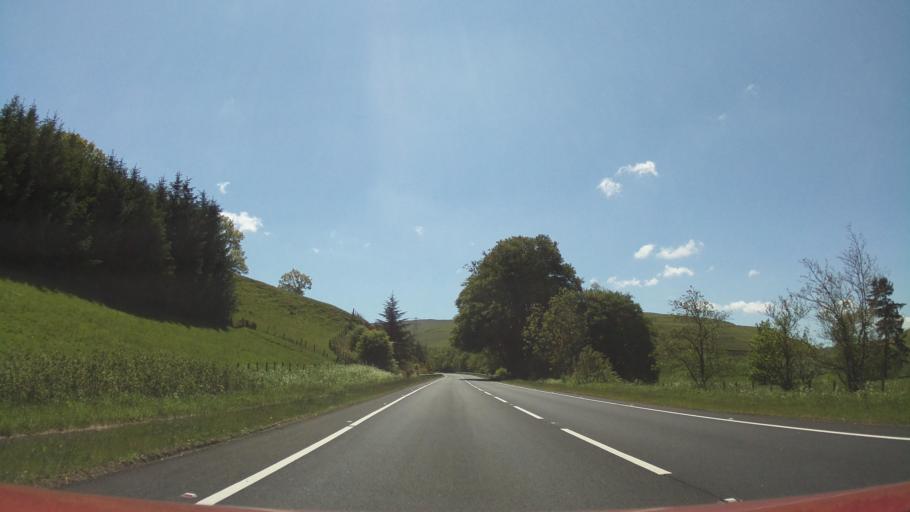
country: GB
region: Scotland
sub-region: The Scottish Borders
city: Hawick
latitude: 55.3314
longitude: -2.9416
